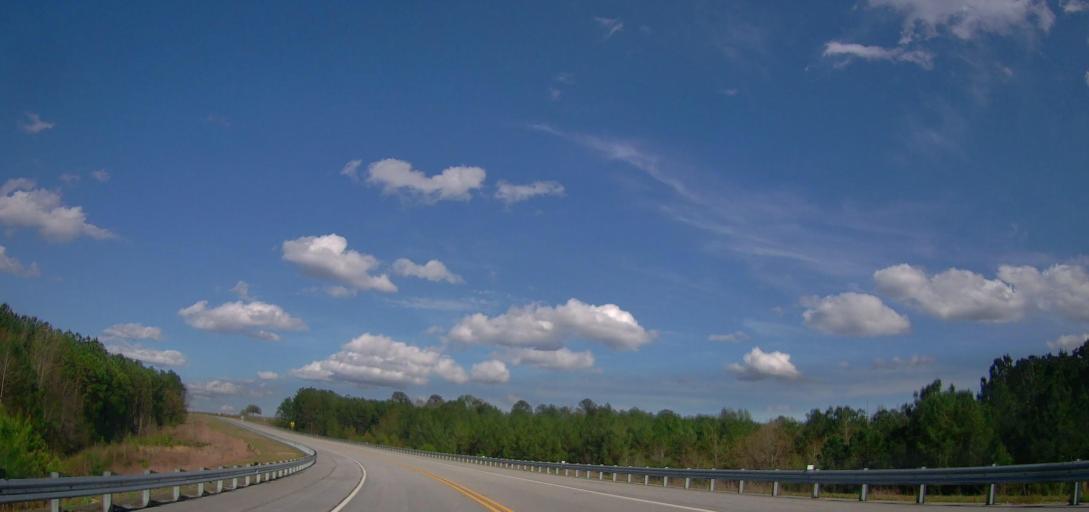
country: US
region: Georgia
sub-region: Baldwin County
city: Hardwick
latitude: 33.0173
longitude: -83.1044
